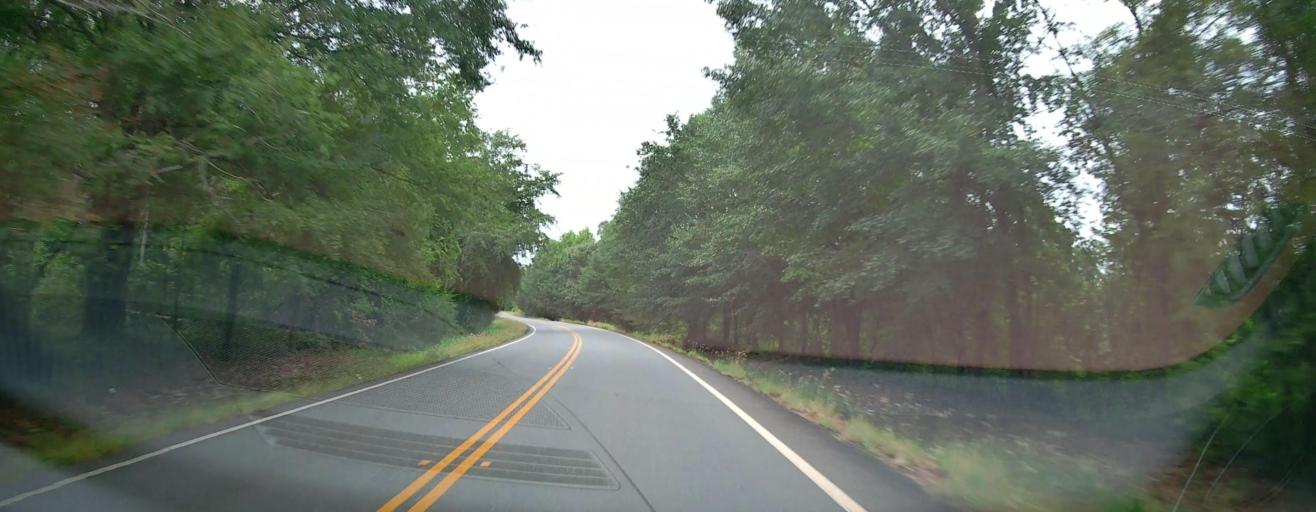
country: US
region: Georgia
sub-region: Marion County
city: Buena Vista
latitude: 32.2766
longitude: -84.4354
